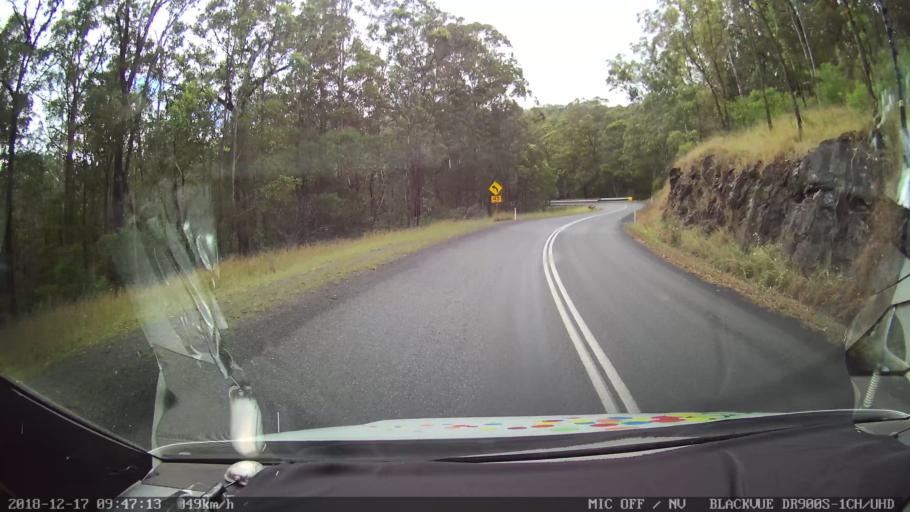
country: AU
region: New South Wales
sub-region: Tenterfield Municipality
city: Carrolls Creek
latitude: -28.9283
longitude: 152.3366
